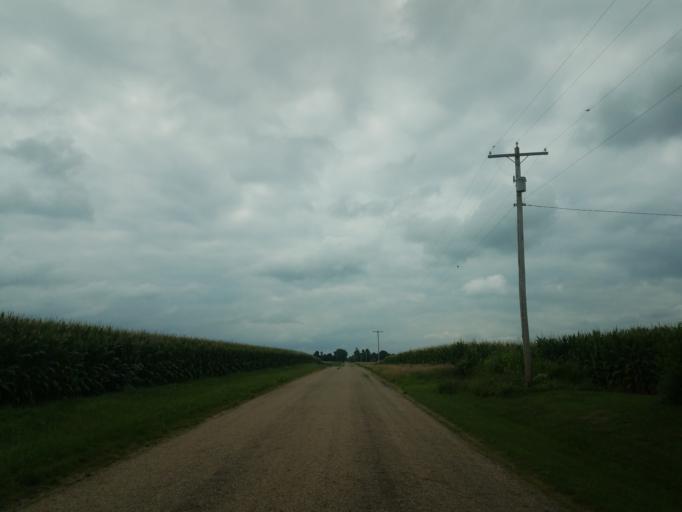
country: US
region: Illinois
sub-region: McLean County
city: Twin Grove
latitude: 40.4223
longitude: -89.0621
